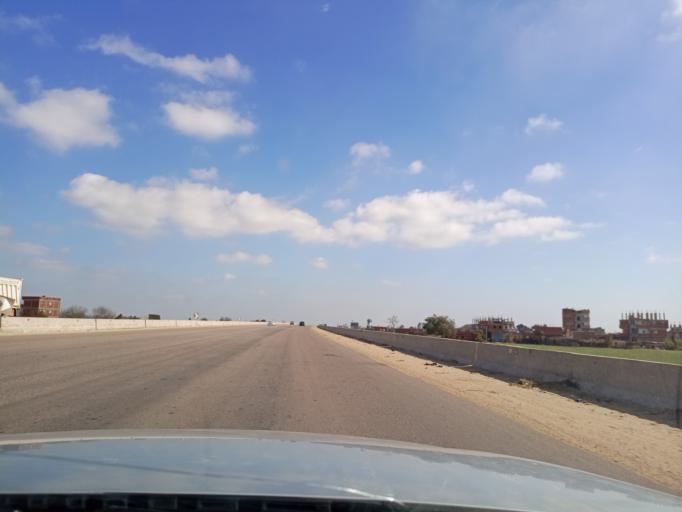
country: EG
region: Muhafazat al Minufiyah
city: Al Bajur
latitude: 30.3930
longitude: 31.0008
